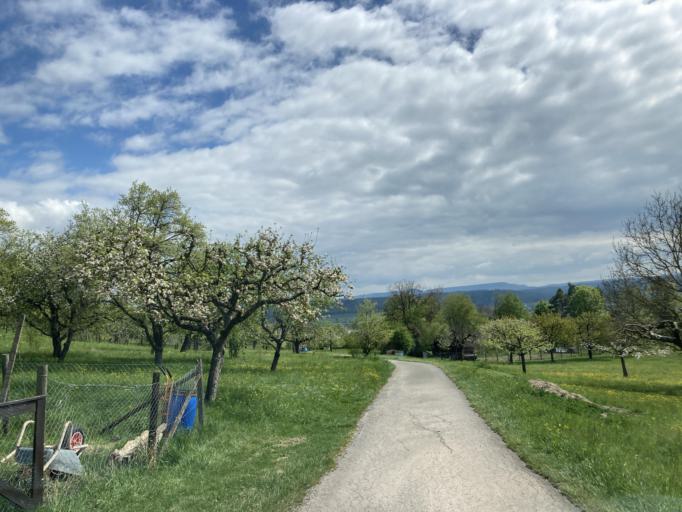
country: DE
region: Baden-Wuerttemberg
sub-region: Tuebingen Region
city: Rottenburg
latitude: 48.5067
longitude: 8.9861
